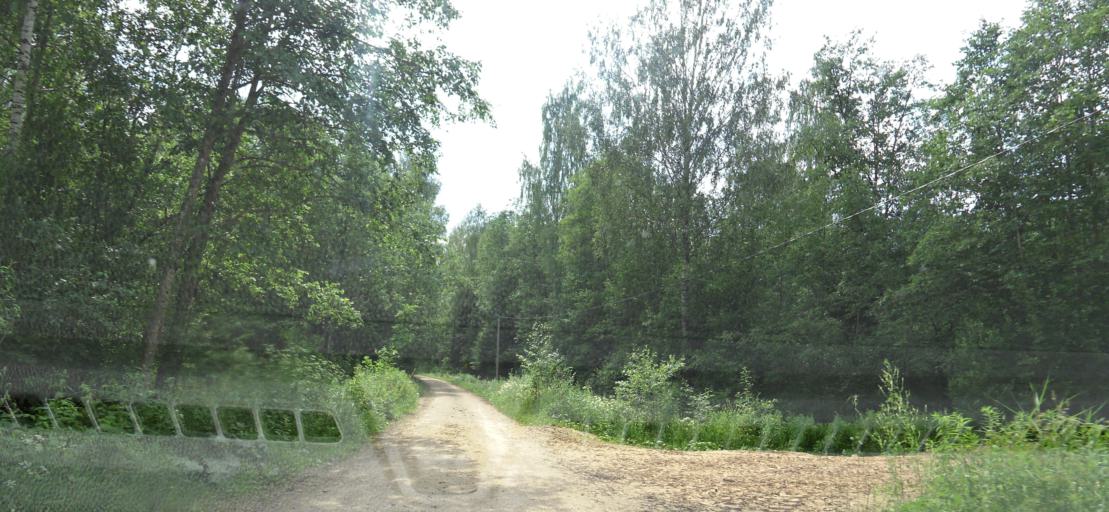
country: LV
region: Ogre
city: Jumprava
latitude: 56.4396
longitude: 24.9057
